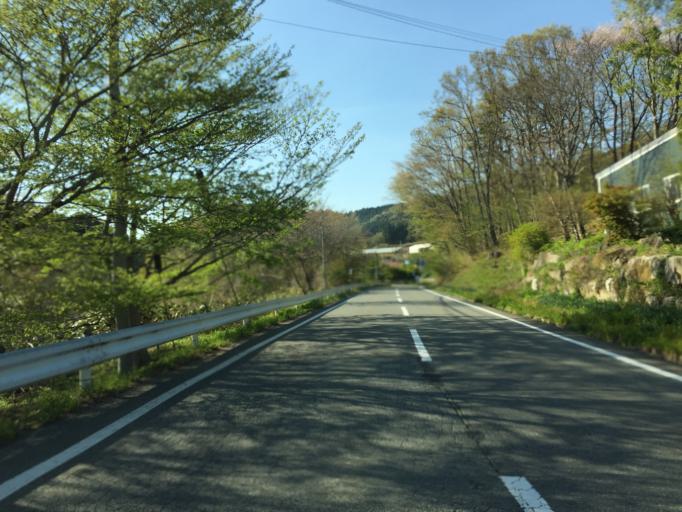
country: JP
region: Fukushima
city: Funehikimachi-funehiki
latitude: 37.5125
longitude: 140.7585
